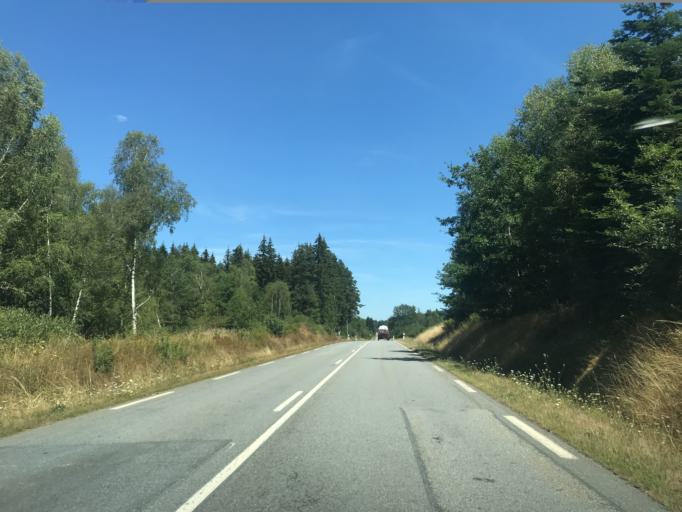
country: FR
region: Limousin
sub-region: Departement de la Correze
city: Meymac
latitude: 45.4942
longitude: 2.2149
